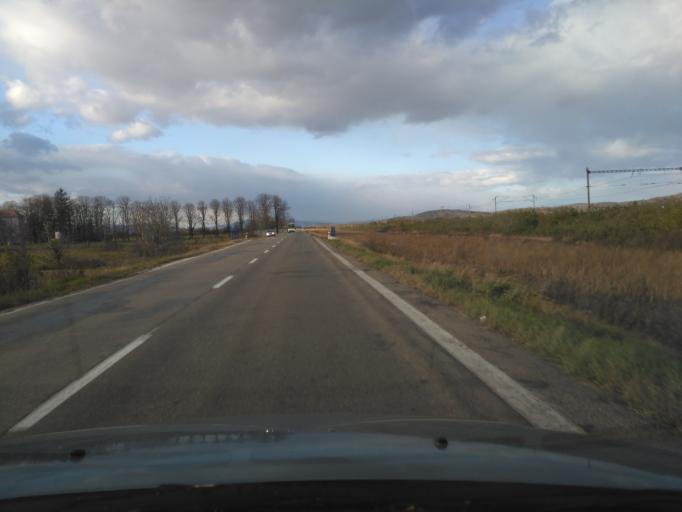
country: HU
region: Borsod-Abauj-Zemplen
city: Satoraljaujhely
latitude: 48.4138
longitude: 21.6652
